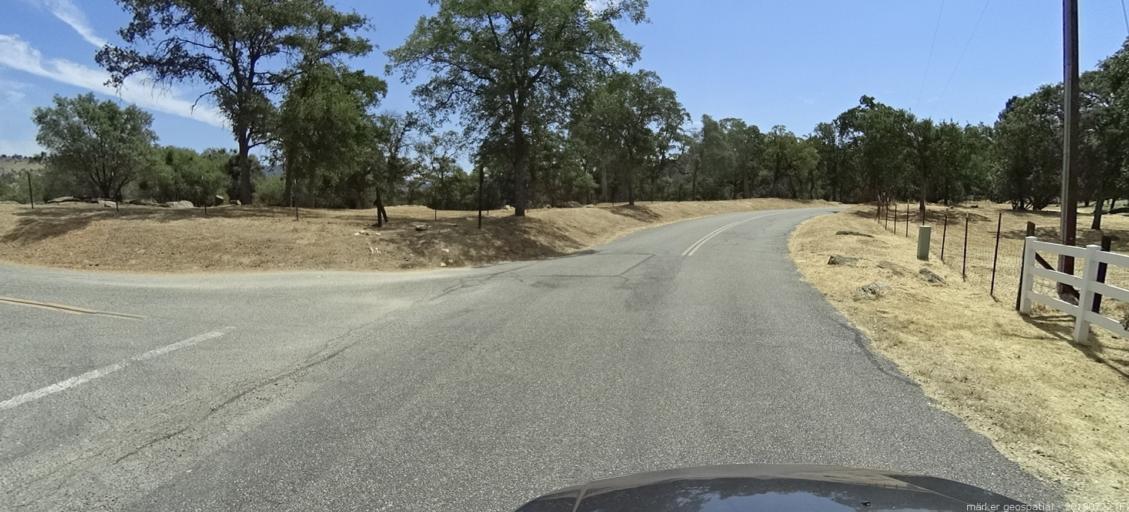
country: US
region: California
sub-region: Madera County
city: Coarsegold
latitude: 37.2825
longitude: -119.7449
